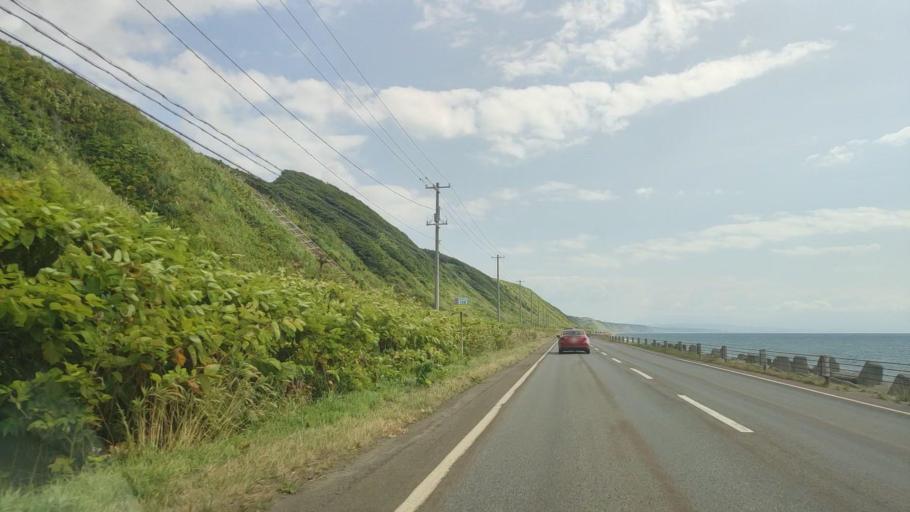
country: JP
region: Hokkaido
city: Rumoi
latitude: 44.0964
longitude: 141.6604
